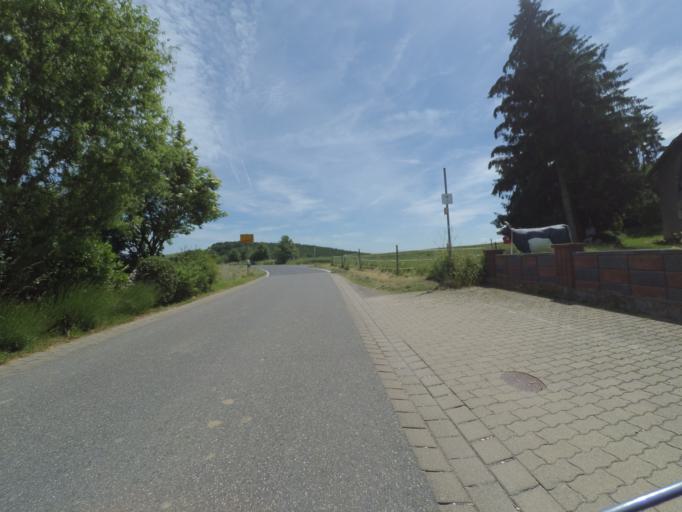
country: DE
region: Rheinland-Pfalz
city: Lonnig
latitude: 50.3097
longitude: 7.4137
